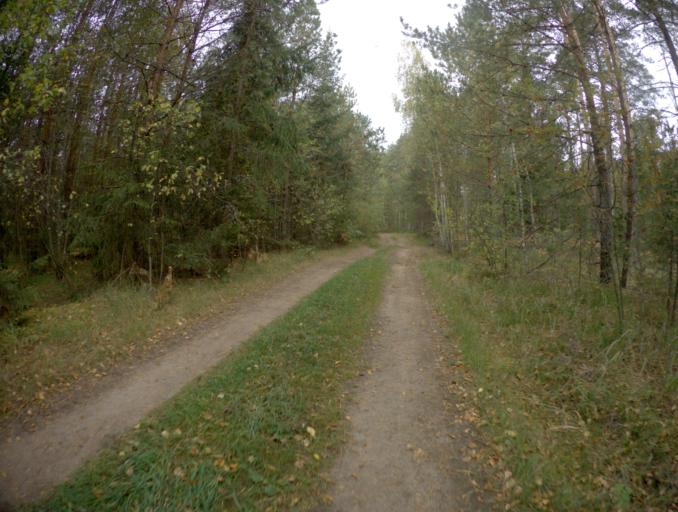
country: RU
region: Moskovskaya
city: Misheronskiy
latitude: 55.7619
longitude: 39.6062
